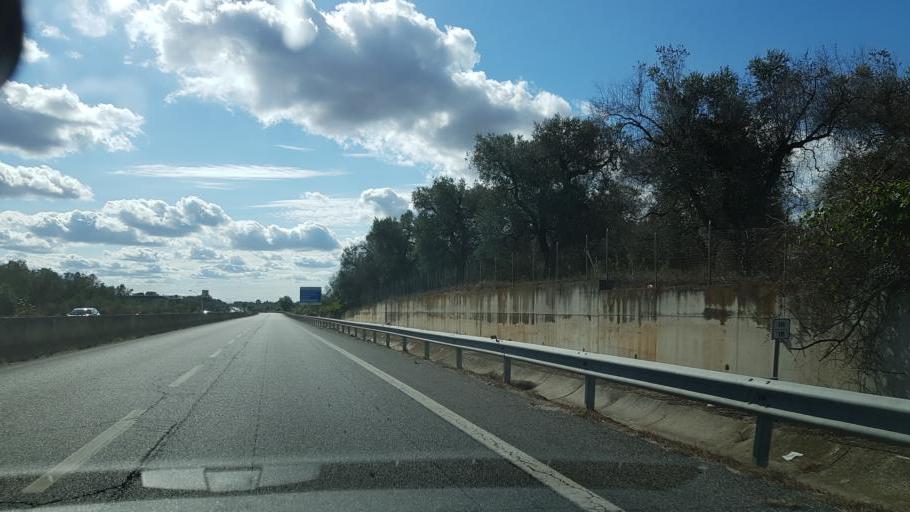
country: IT
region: Apulia
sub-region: Provincia di Brindisi
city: Torchiarolo
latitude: 40.4927
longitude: 18.0370
